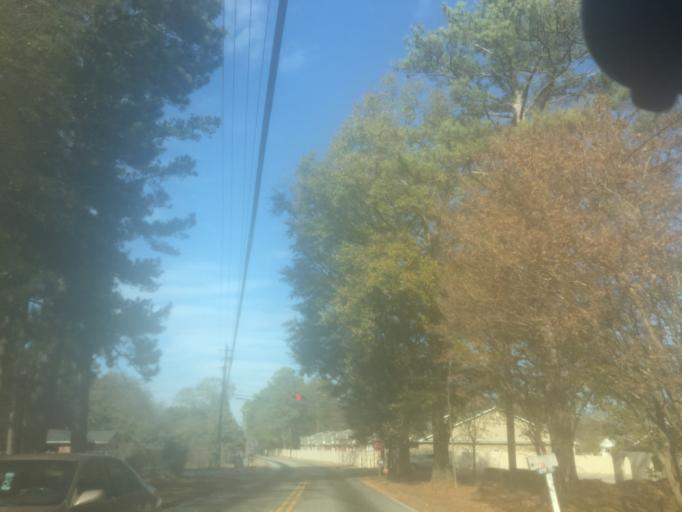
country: US
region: Georgia
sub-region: Clayton County
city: Riverdale
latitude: 33.5660
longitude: -84.4160
